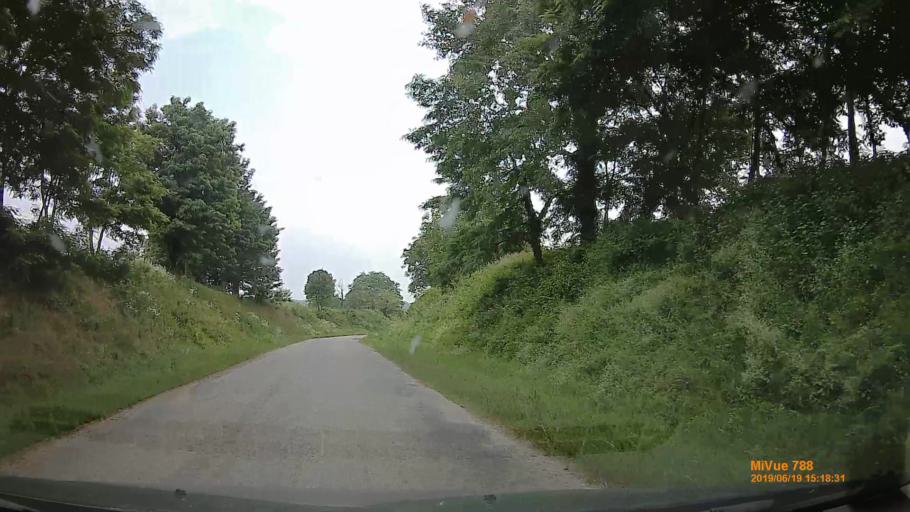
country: HU
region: Baranya
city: Szigetvar
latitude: 46.0763
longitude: 17.8566
